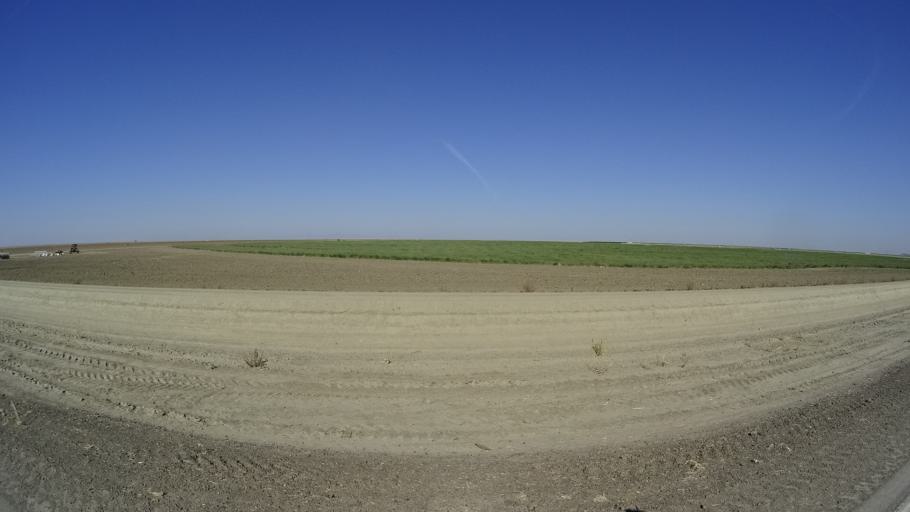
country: US
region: California
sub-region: Kings County
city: Corcoran
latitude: 36.0522
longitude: -119.5721
